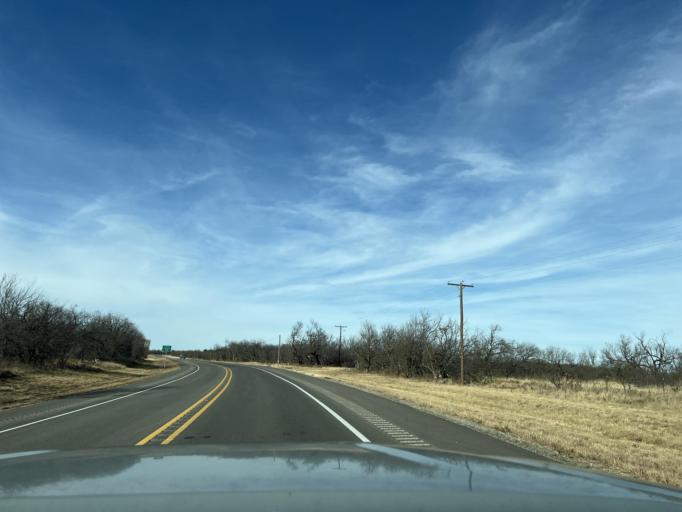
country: US
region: Texas
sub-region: Shackelford County
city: Albany
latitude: 32.5723
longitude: -99.1770
